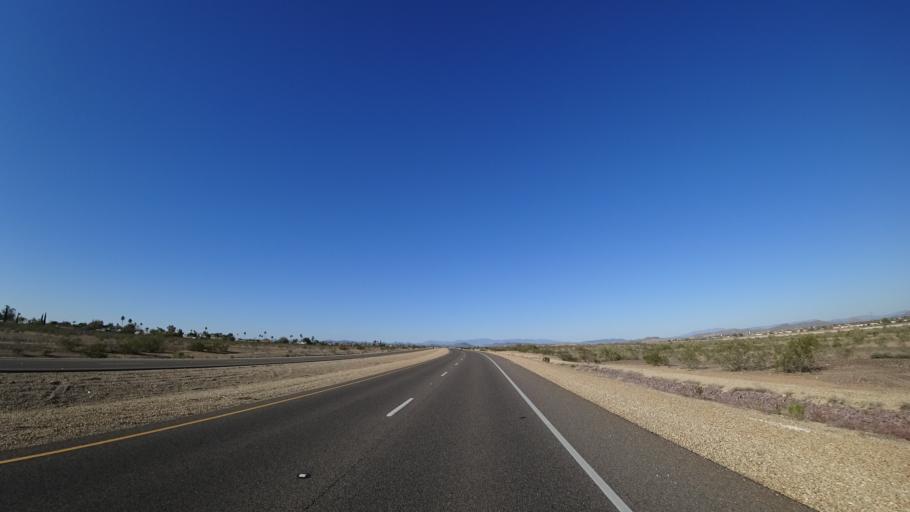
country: US
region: Arizona
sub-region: Maricopa County
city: Sun City West
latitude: 33.6501
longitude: -112.3226
